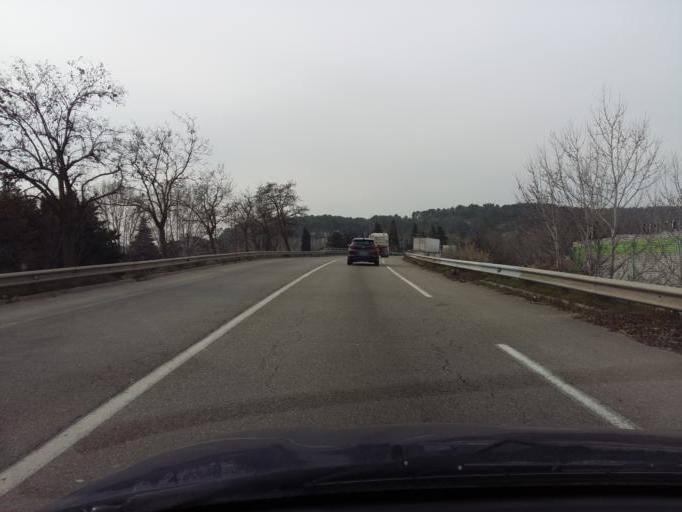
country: FR
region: Provence-Alpes-Cote d'Azur
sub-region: Departement des Bouches-du-Rhone
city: Noves
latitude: 43.8859
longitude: 4.8962
